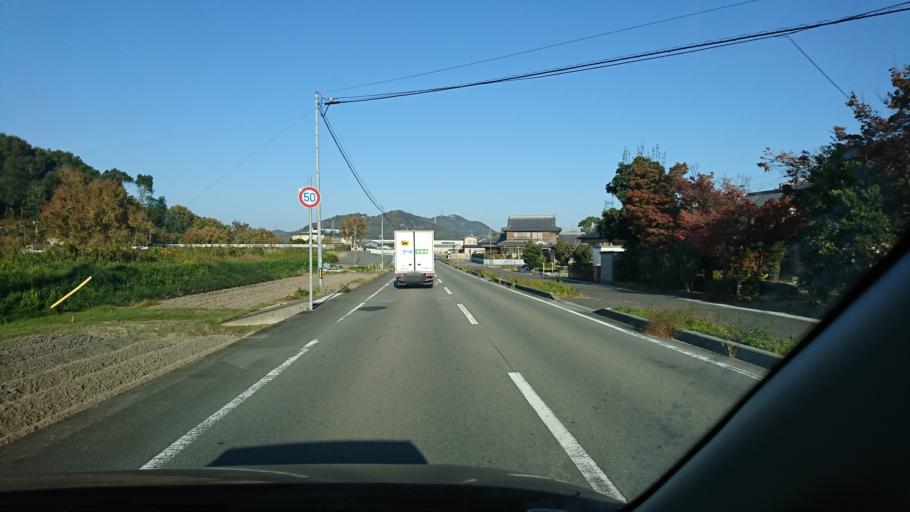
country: JP
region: Hyogo
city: Kakogawacho-honmachi
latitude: 34.7837
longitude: 134.8711
